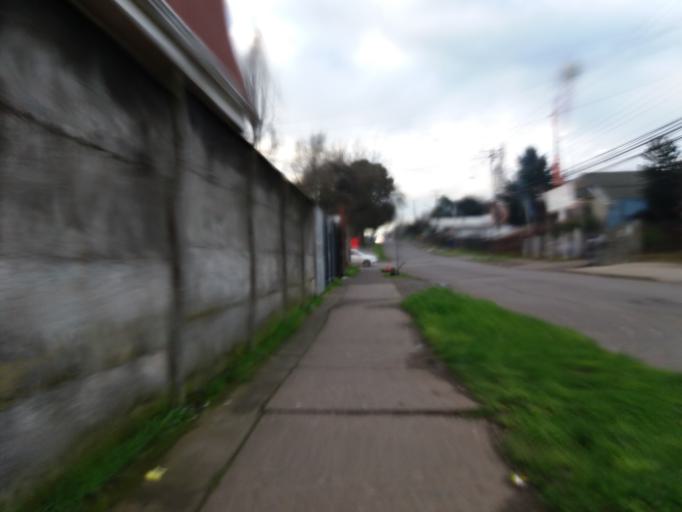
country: CL
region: Araucania
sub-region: Provincia de Cautin
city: Temuco
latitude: -38.7470
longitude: -72.6048
